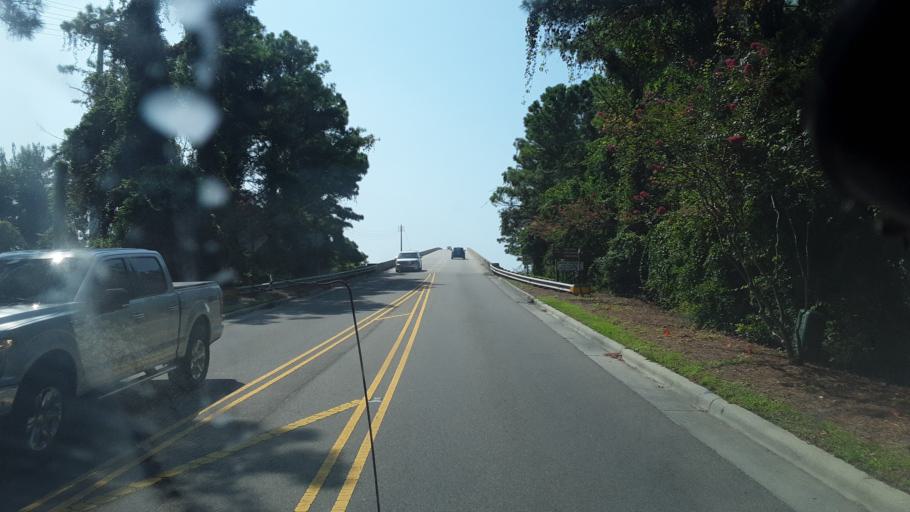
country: US
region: North Carolina
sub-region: Brunswick County
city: Sunset Beach
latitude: 33.8990
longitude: -78.4406
